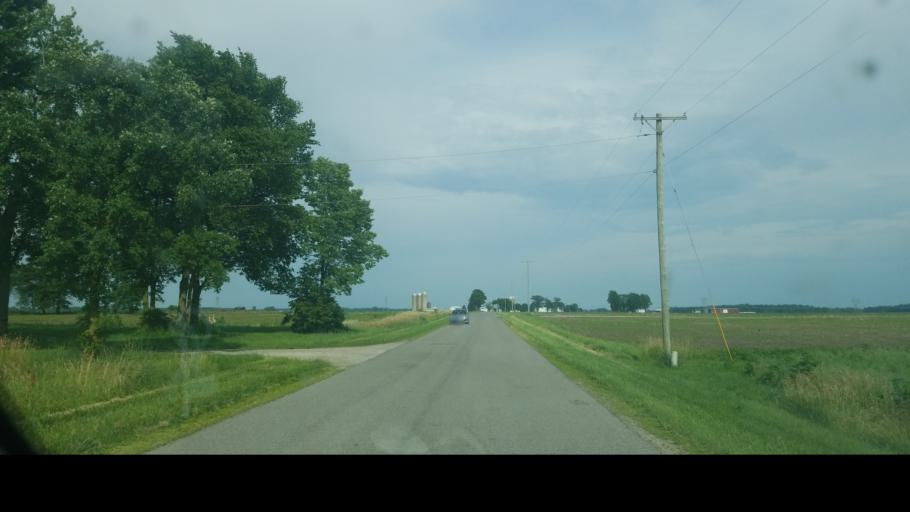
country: US
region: Ohio
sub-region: Union County
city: Marysville
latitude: 40.1564
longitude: -83.4380
